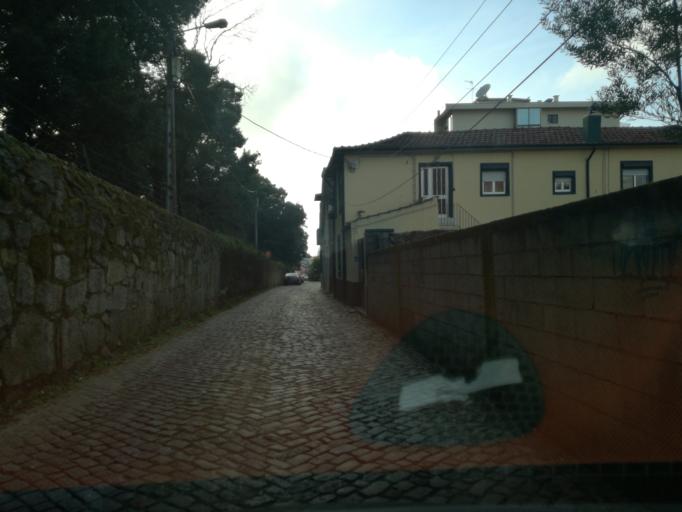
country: PT
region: Porto
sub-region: Matosinhos
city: Senhora da Hora
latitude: 41.1758
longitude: -8.6290
